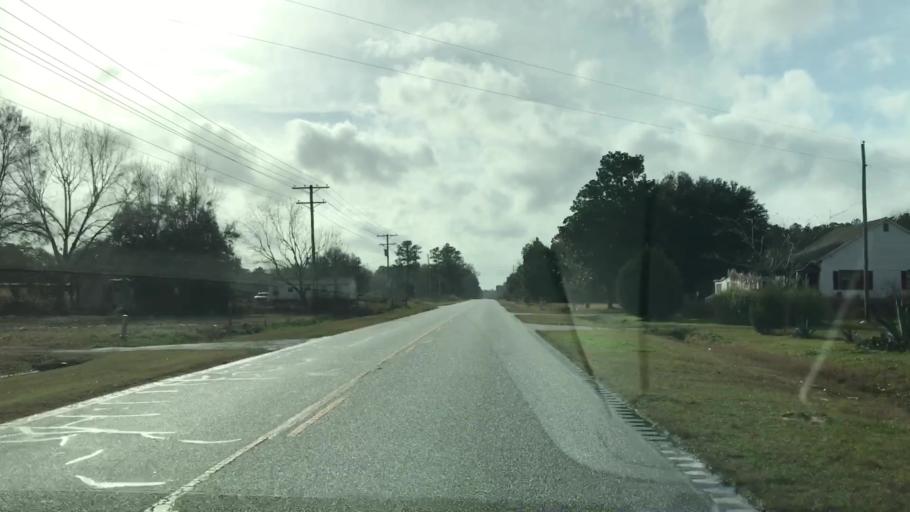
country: US
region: South Carolina
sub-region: Williamsburg County
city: Andrews
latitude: 33.5026
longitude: -79.5262
